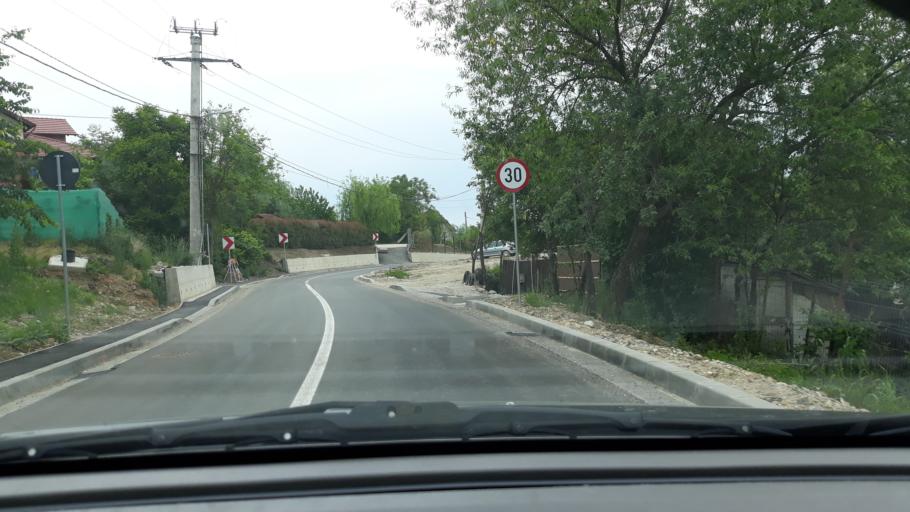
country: RO
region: Bihor
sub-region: Comuna Osorheiu
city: Osorheiu
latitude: 47.0588
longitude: 22.0176
